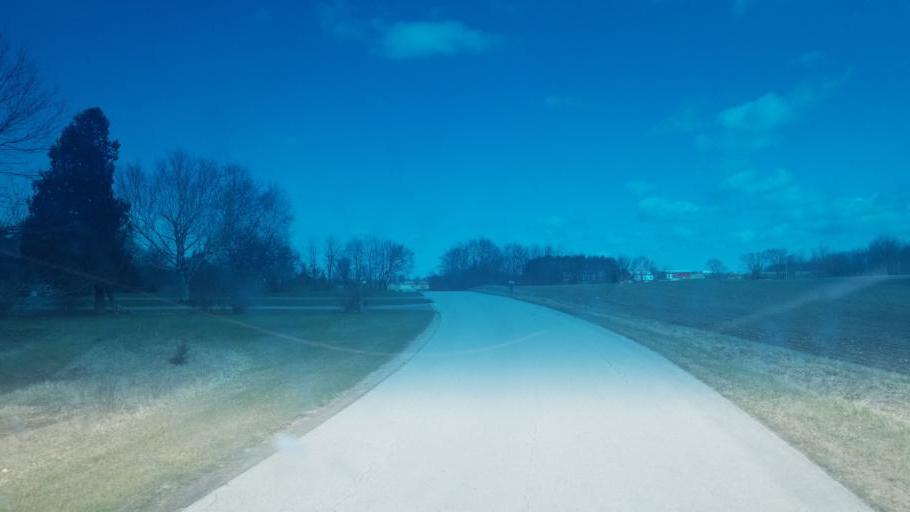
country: US
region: Ohio
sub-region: Crawford County
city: Bucyrus
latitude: 40.8163
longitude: -83.0739
